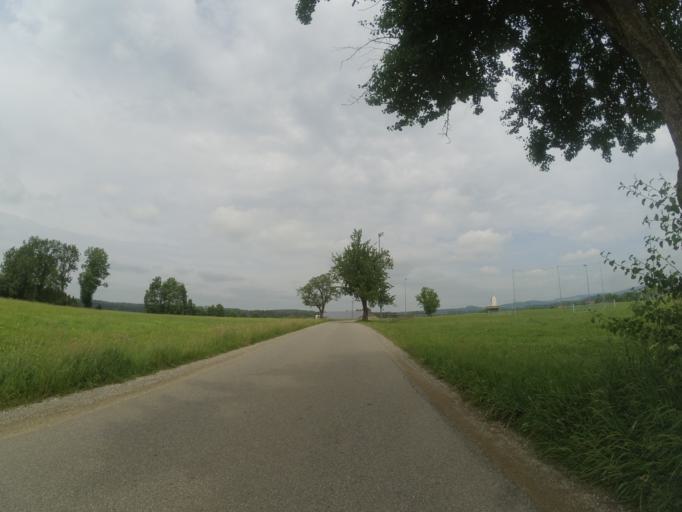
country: DE
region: Baden-Wuerttemberg
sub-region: Tuebingen Region
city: Isny im Allgau
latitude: 47.7462
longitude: 10.0133
